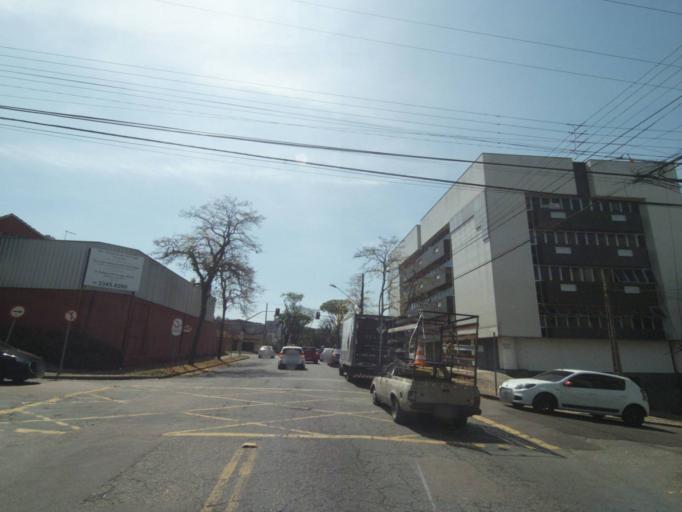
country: BR
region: Parana
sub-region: Curitiba
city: Curitiba
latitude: -25.4749
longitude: -49.2881
